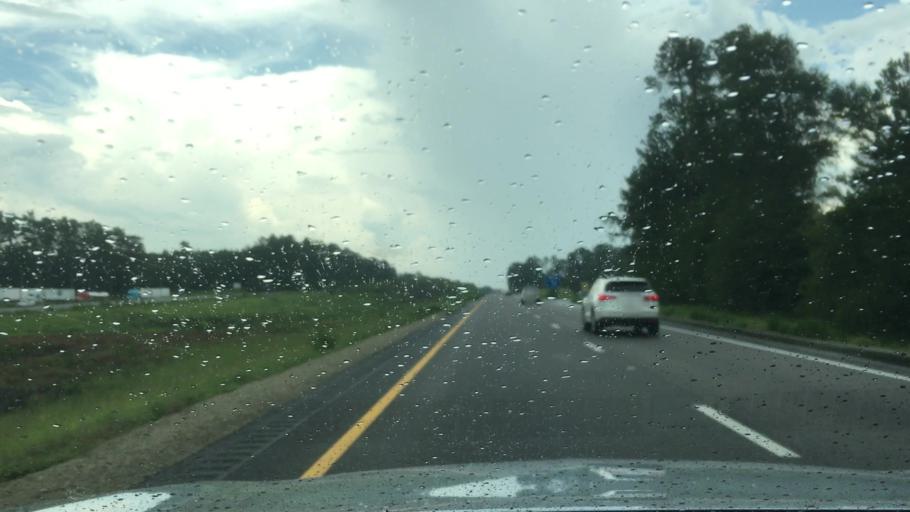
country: US
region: Mississippi
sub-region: Lamar County
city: Purvis
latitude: 31.1984
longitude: -89.3383
